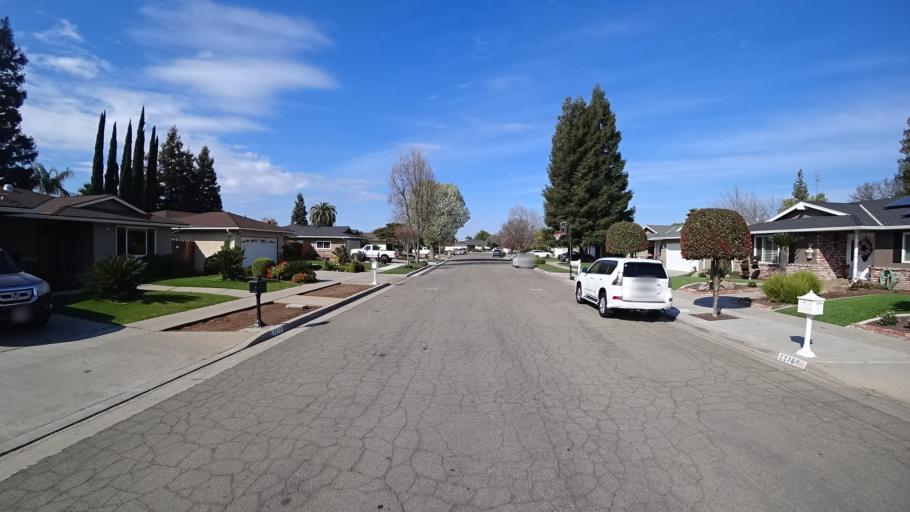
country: US
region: California
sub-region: Fresno County
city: Clovis
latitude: 36.8365
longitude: -119.7490
